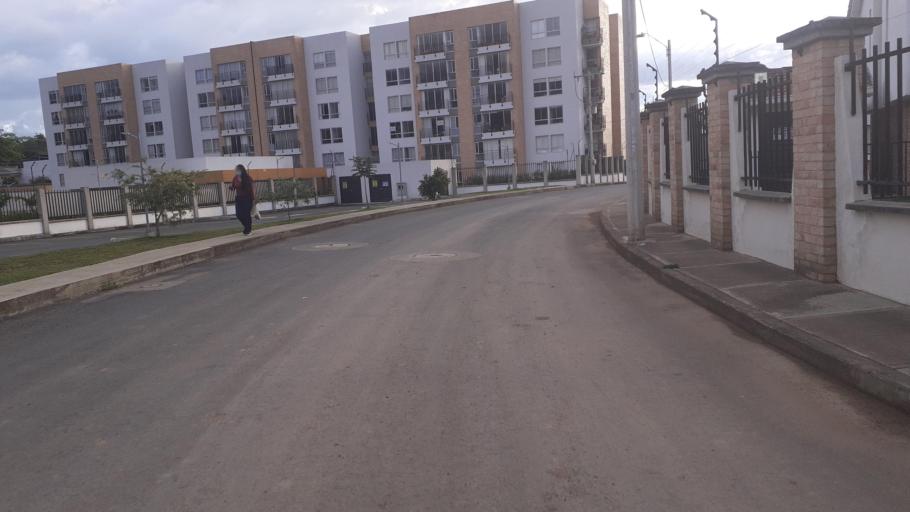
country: CO
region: Cauca
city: Popayan
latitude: 2.4633
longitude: -76.5832
